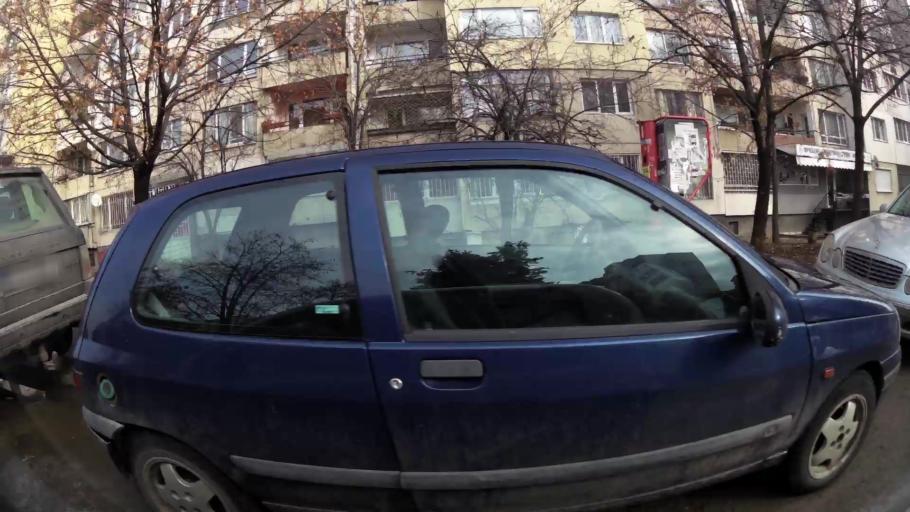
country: BG
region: Sofia-Capital
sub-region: Stolichna Obshtina
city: Sofia
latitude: 42.7135
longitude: 23.2704
